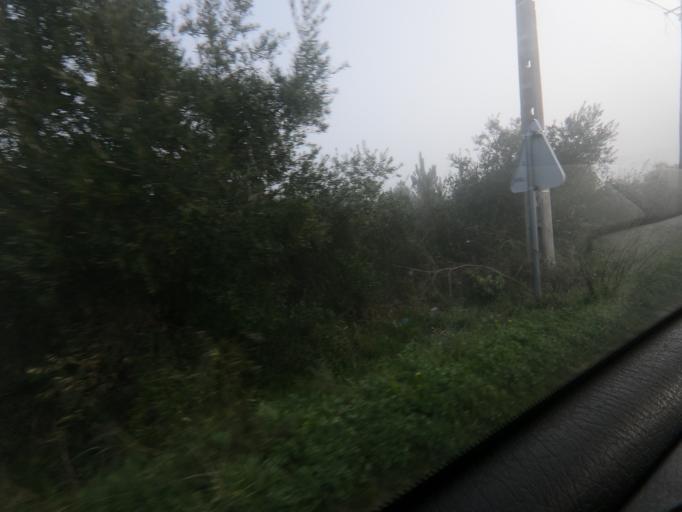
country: PT
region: Setubal
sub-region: Palmela
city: Palmela
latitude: 38.6083
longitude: -8.8612
